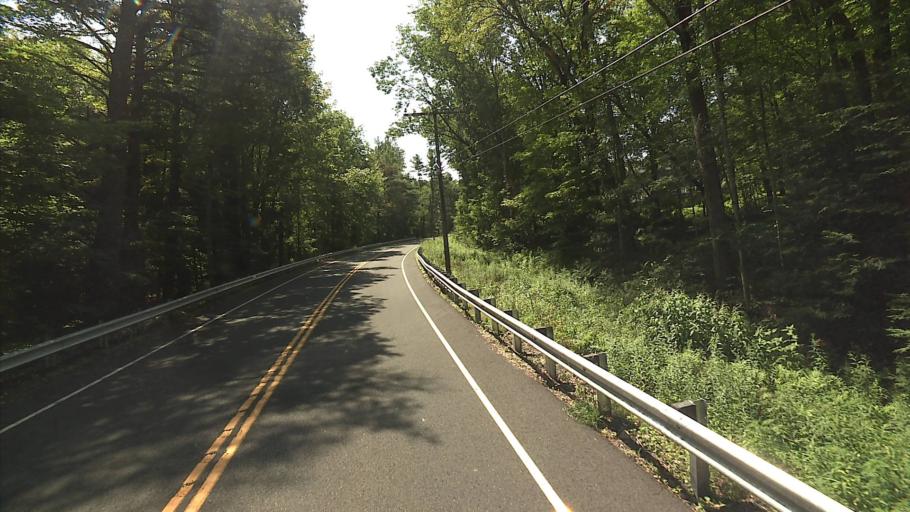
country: US
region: Massachusetts
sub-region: Berkshire County
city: New Marlborough
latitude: 42.0348
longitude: -73.2078
